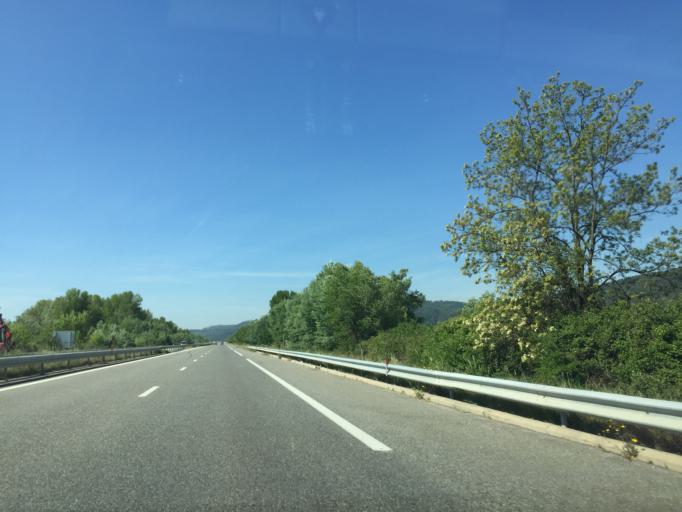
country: FR
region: Provence-Alpes-Cote d'Azur
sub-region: Departement des Alpes-de-Haute-Provence
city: Peyruis
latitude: 44.0257
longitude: 5.9518
